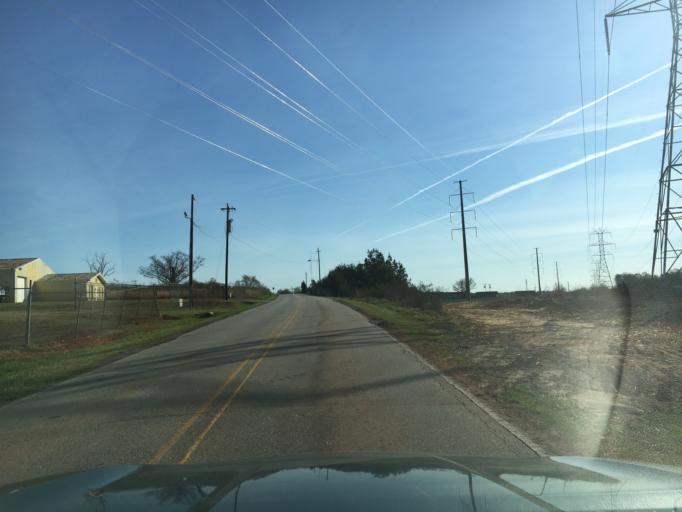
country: US
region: South Carolina
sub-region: Spartanburg County
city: Duncan
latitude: 34.9557
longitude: -82.1770
